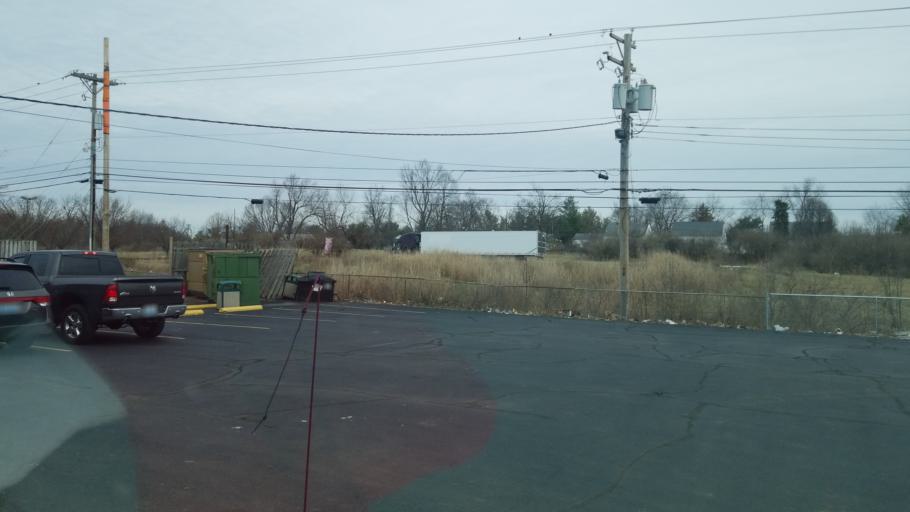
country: US
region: Kentucky
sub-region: Fayette County
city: Lexington-Fayette
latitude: 38.0621
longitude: -84.4662
